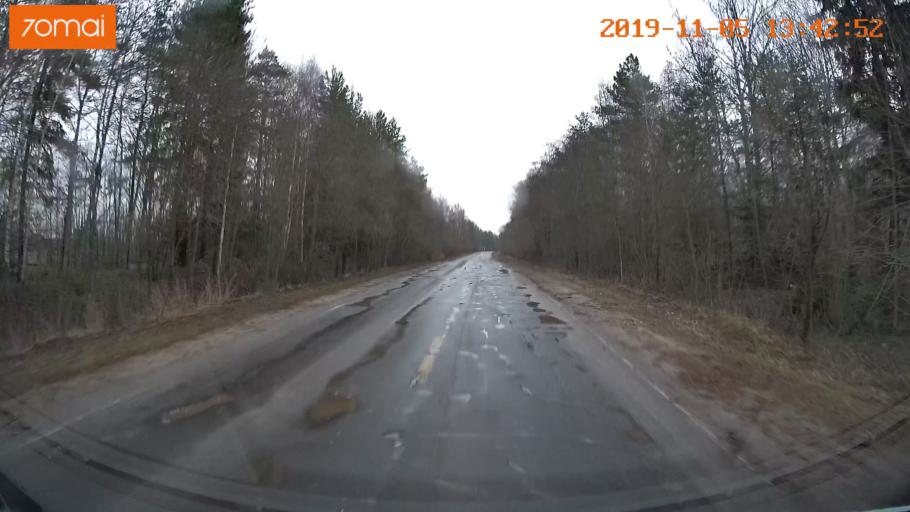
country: RU
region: Ivanovo
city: Shuya
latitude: 56.9695
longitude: 41.3985
